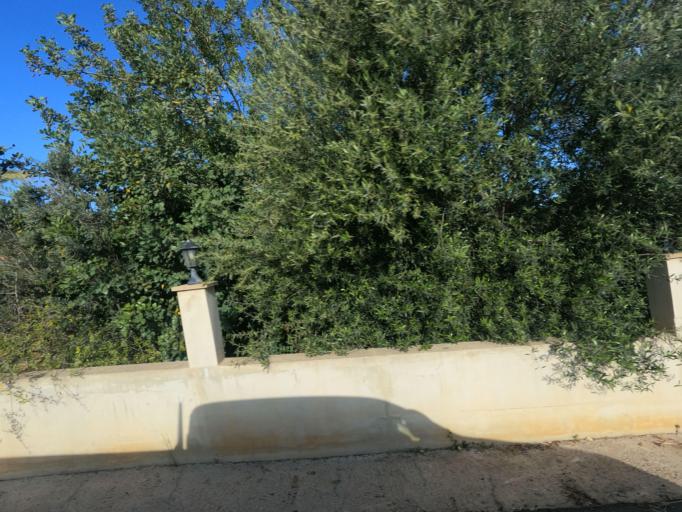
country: CY
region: Pafos
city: Polis
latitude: 35.0342
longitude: 32.3777
